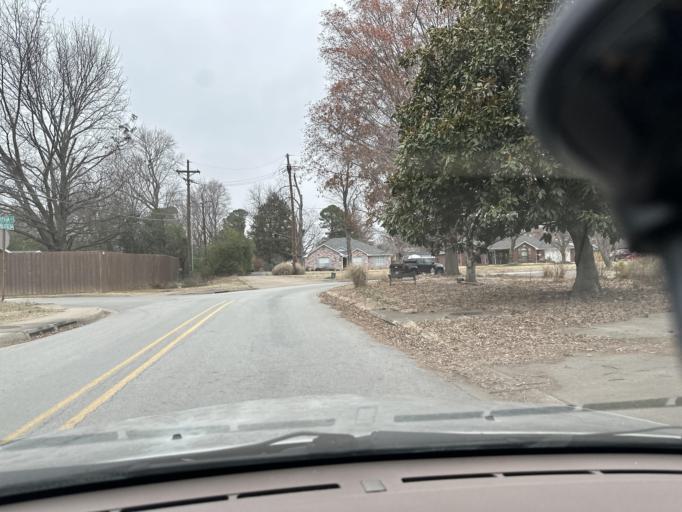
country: US
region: Arkansas
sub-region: Washington County
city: Johnson
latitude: 36.1103
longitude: -94.1406
